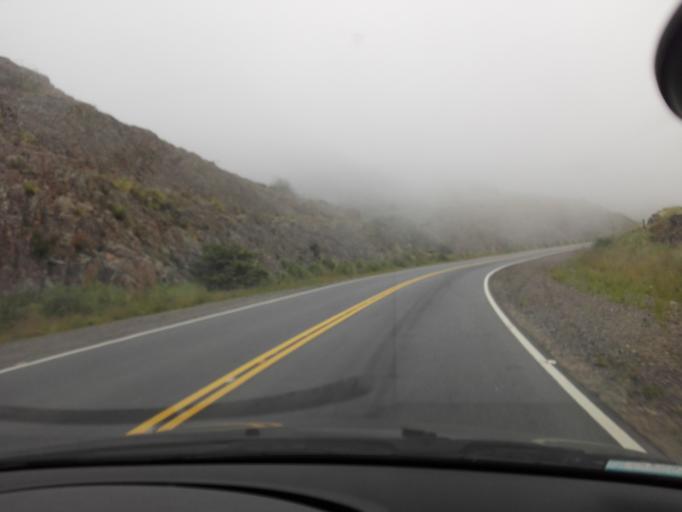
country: AR
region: Cordoba
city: Cuesta Blanca
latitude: -31.6048
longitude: -64.7026
